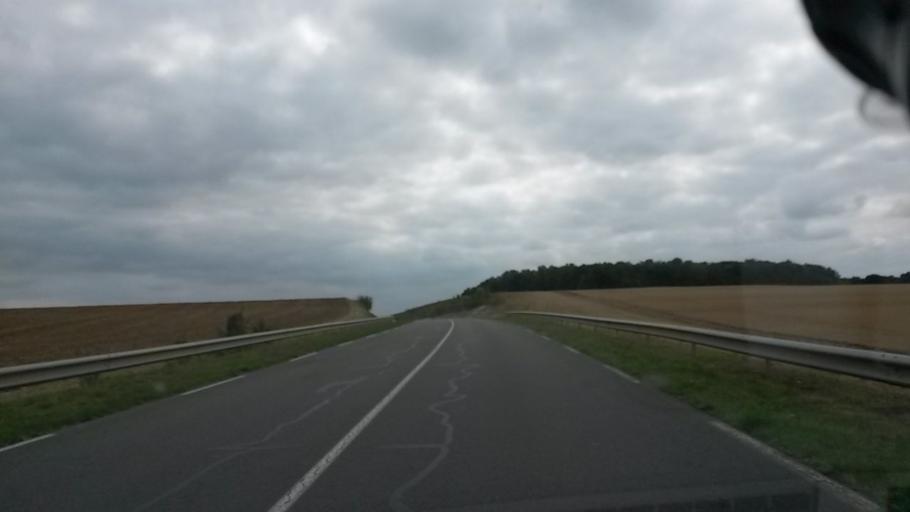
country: FR
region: Picardie
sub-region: Departement de la Somme
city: Camon
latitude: 49.9389
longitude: 2.4127
